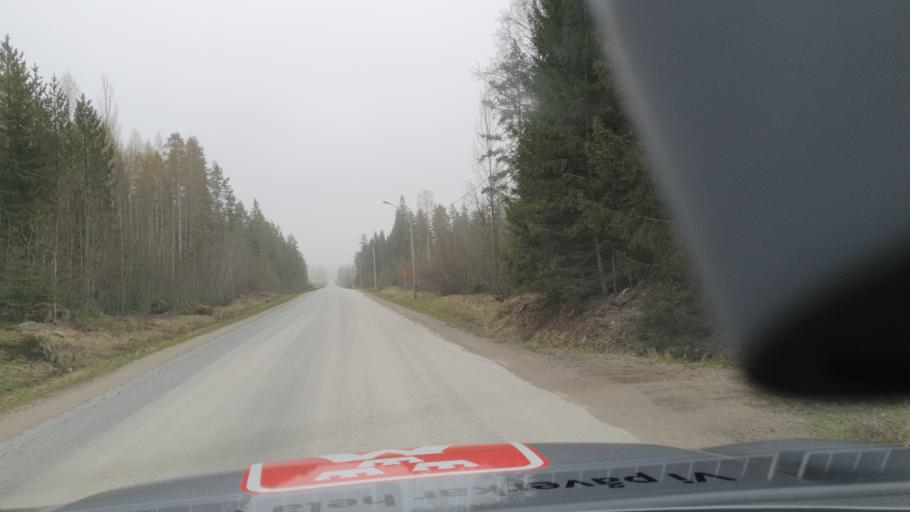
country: SE
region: Vaesternorrland
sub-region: OErnskoeldsviks Kommun
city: Husum
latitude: 63.5900
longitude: 19.0173
